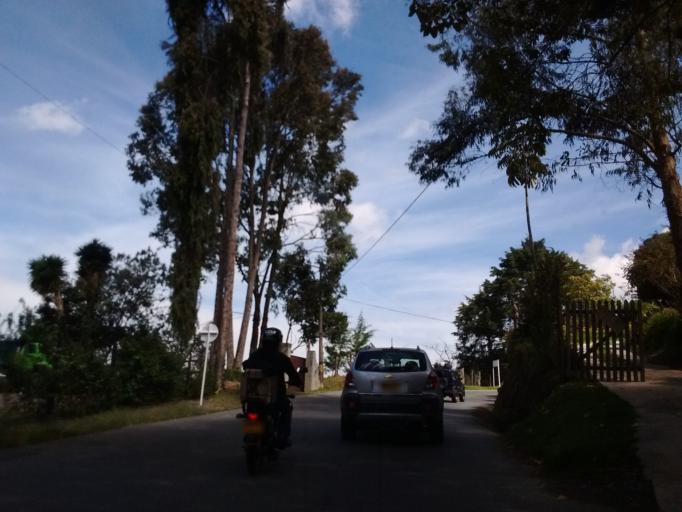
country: CO
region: Antioquia
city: Medellin
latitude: 6.2421
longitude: -75.5135
